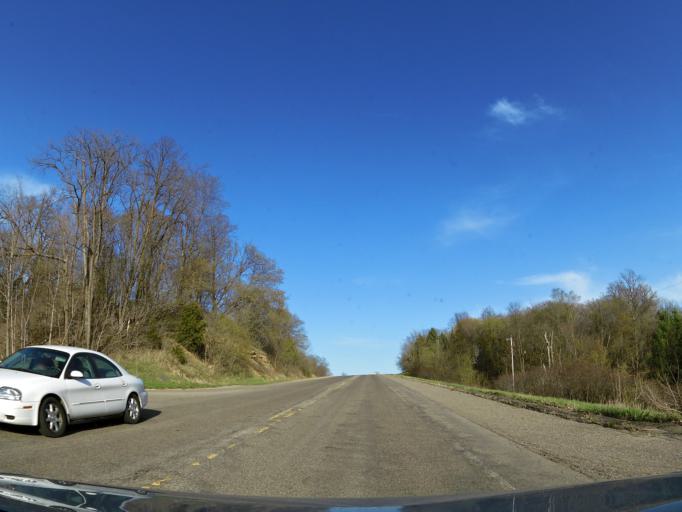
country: US
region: Wisconsin
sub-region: Pierce County
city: River Falls
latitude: 44.8623
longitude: -92.6953
